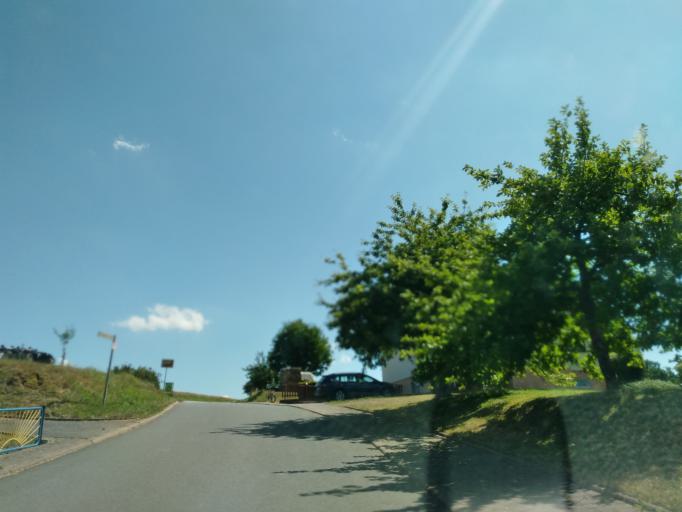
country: DE
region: Baden-Wuerttemberg
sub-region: Karlsruhe Region
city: Limbach
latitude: 49.4820
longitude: 9.2406
